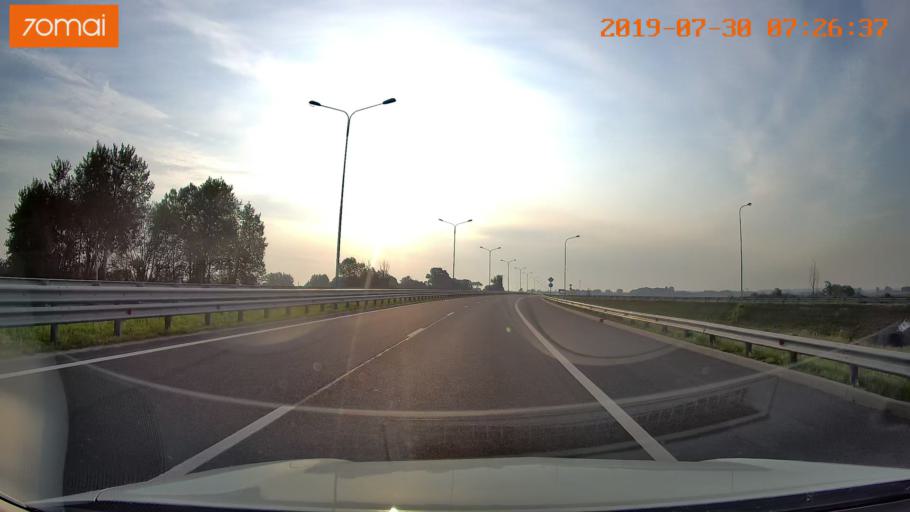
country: RU
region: Kaliningrad
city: Gvardeysk
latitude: 54.6837
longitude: 20.8664
